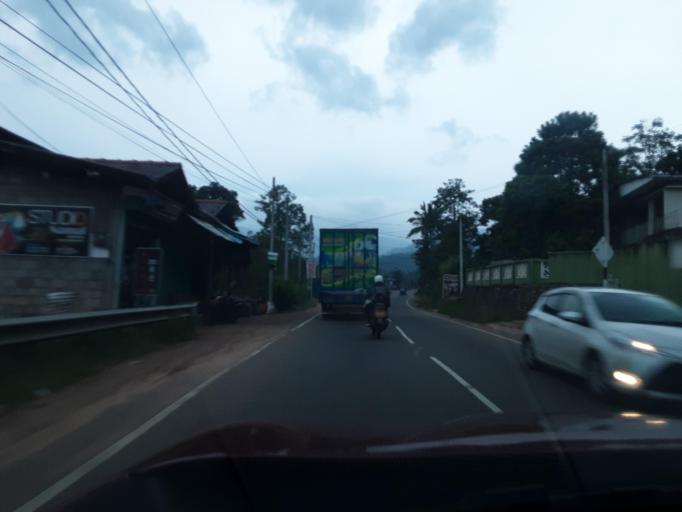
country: LK
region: Central
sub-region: Nuwara Eliya District
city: Nuwara Eliya
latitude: 6.9023
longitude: 80.8954
